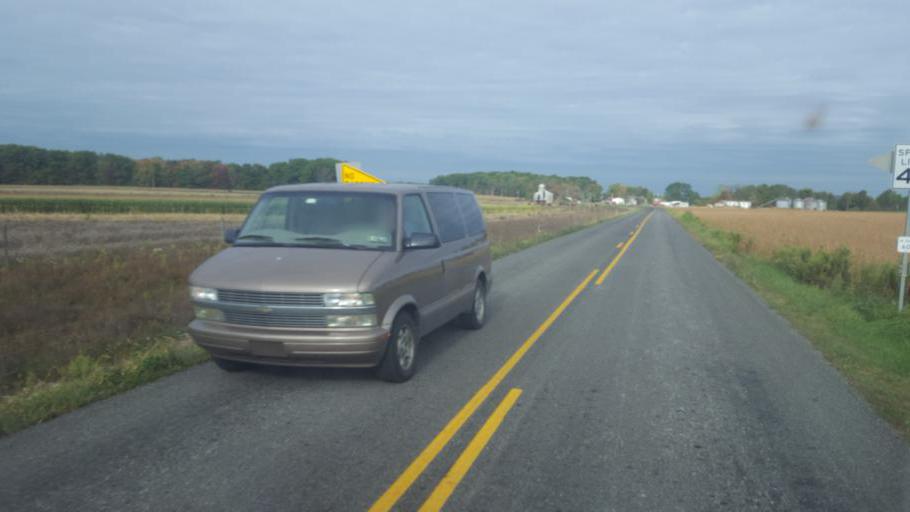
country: US
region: Pennsylvania
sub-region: Mercer County
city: Reynolds Heights
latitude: 41.3446
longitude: -80.2806
